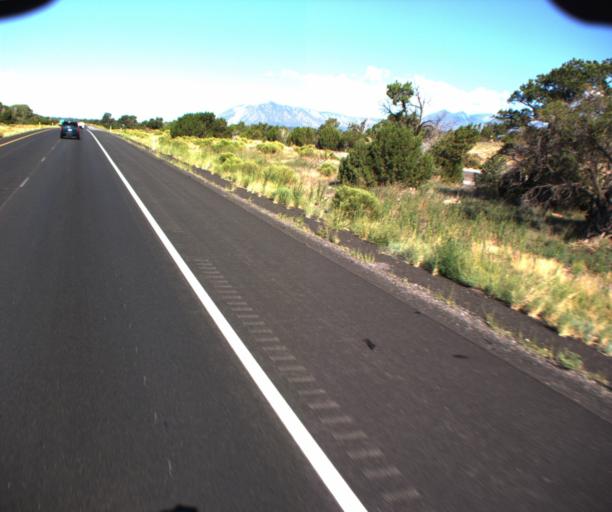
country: US
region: Arizona
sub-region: Coconino County
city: Flagstaff
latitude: 35.2027
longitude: -111.4601
